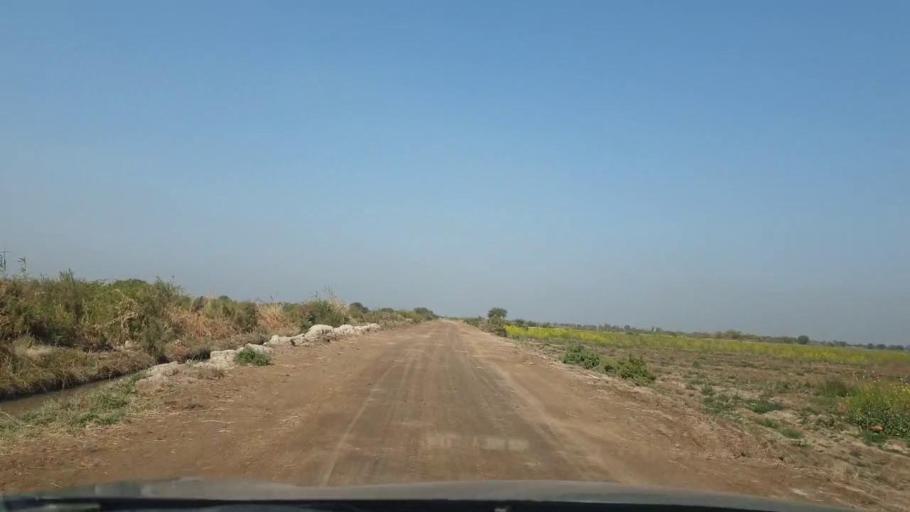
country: PK
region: Sindh
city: Berani
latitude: 25.7096
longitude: 68.8617
